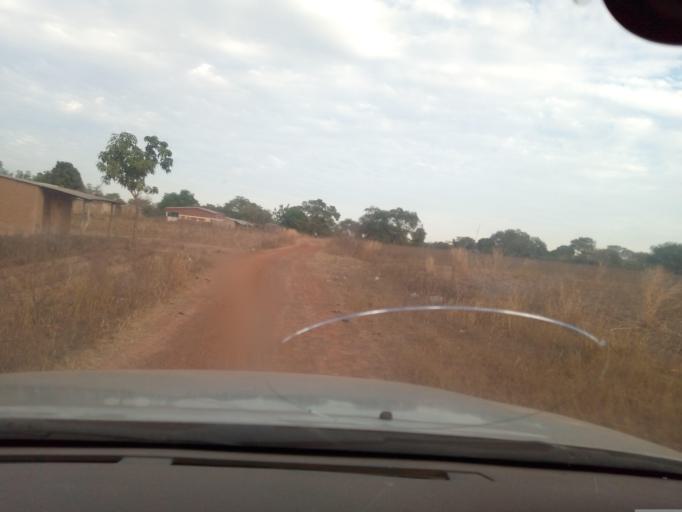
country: ML
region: Sikasso
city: Kadiolo
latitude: 10.5843
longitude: -5.8472
